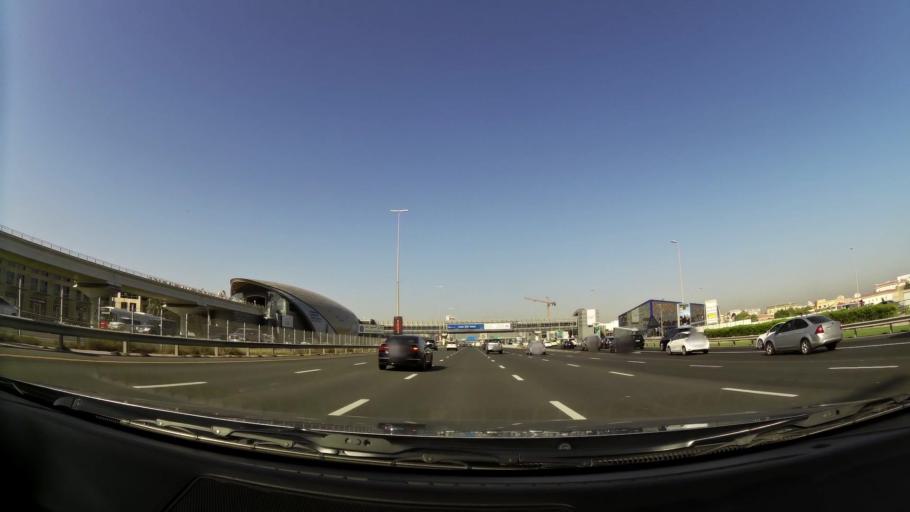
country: AE
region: Dubai
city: Dubai
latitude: 25.1279
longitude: 55.2086
